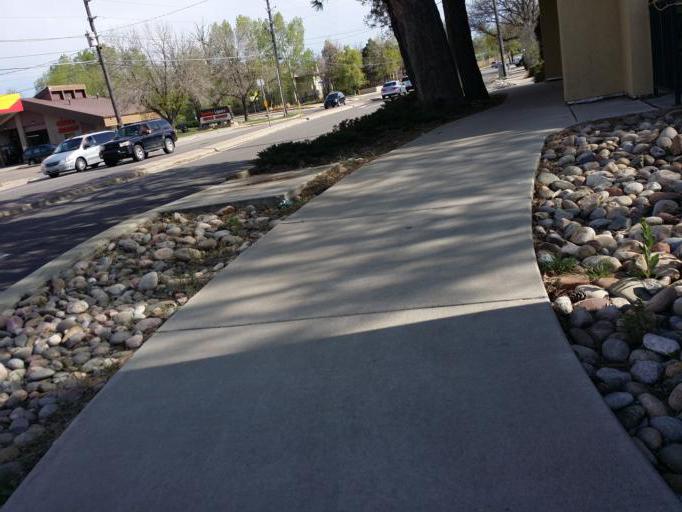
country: US
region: Colorado
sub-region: Boulder County
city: Boulder
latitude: 40.0000
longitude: -105.2603
